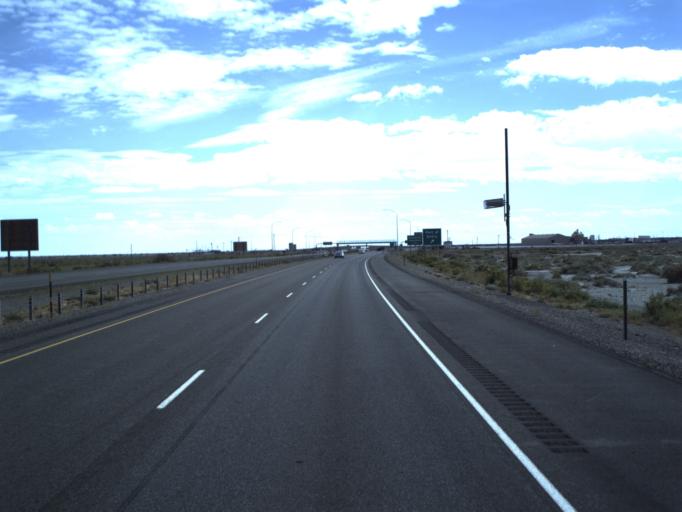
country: US
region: Utah
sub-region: Tooele County
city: Wendover
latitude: 40.7466
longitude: -113.9991
